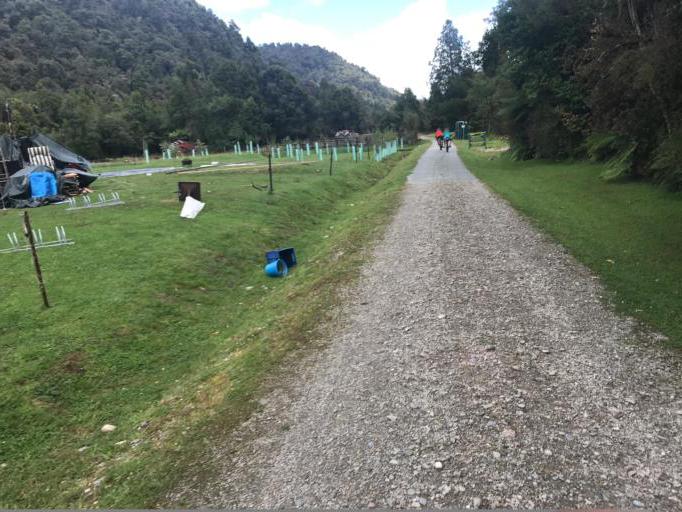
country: NZ
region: West Coast
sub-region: Westland District
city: Hokitika
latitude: -42.7601
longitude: 171.2398
